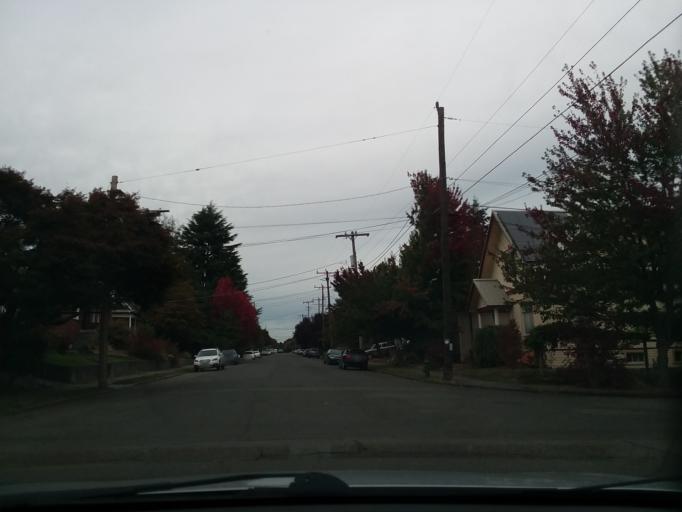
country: US
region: Washington
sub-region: King County
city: Seattle
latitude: 47.6579
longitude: -122.3446
